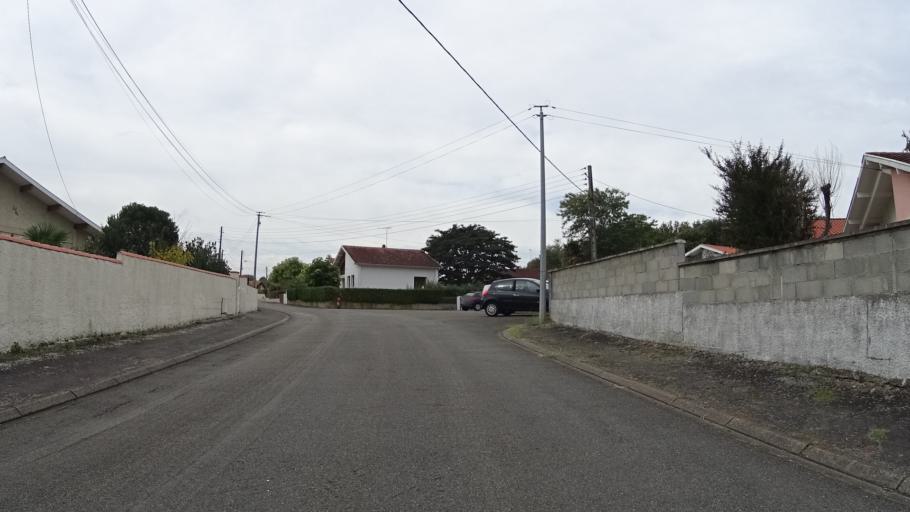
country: FR
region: Aquitaine
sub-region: Departement des Landes
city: Saint-Paul-les-Dax
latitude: 43.7303
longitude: -1.0736
